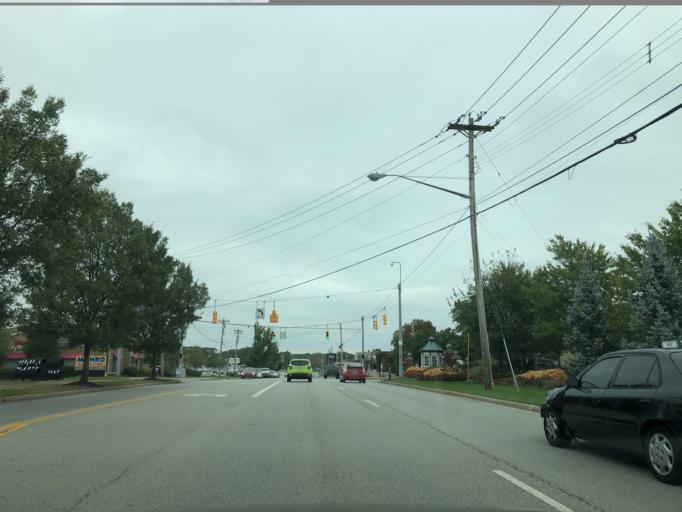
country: US
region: Ohio
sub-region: Hamilton County
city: Montgomery
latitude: 39.2345
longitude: -84.3511
